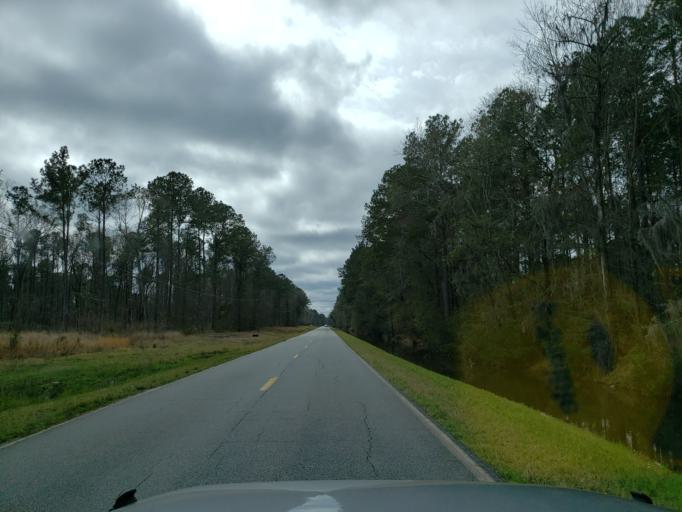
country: US
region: Georgia
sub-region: Chatham County
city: Pooler
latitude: 32.0428
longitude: -81.2949
